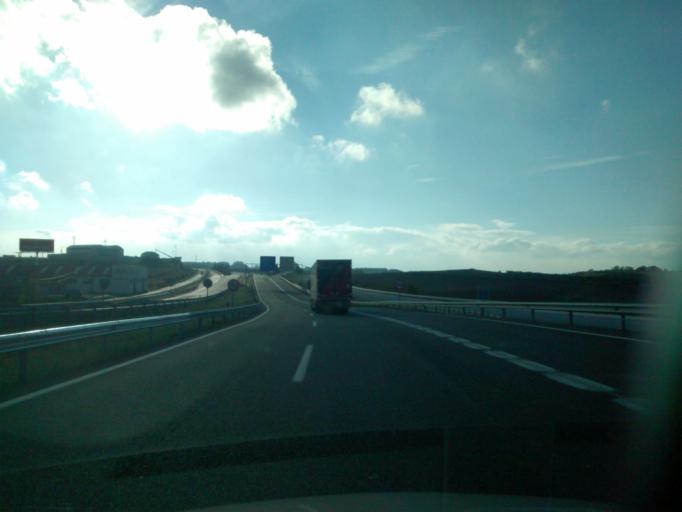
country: ES
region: Castille-La Mancha
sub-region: Provincia de Guadalajara
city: Guadalajara
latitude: 40.6493
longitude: -3.1332
